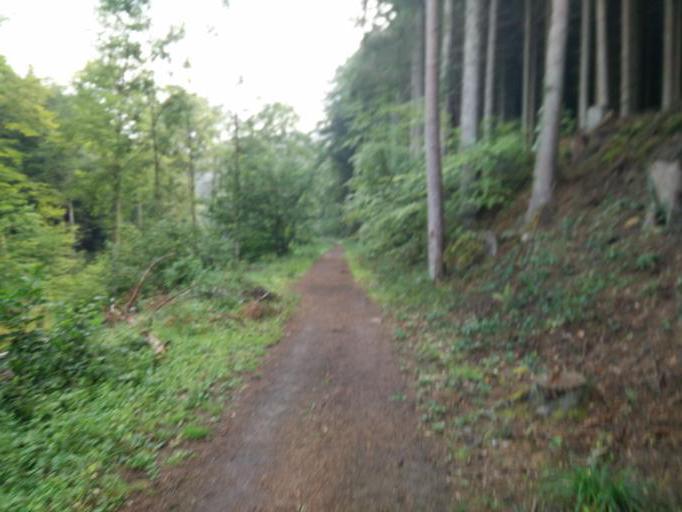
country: LU
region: Luxembourg
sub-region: Canton de Luxembourg
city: Bertrange
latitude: 49.6360
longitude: 6.0480
